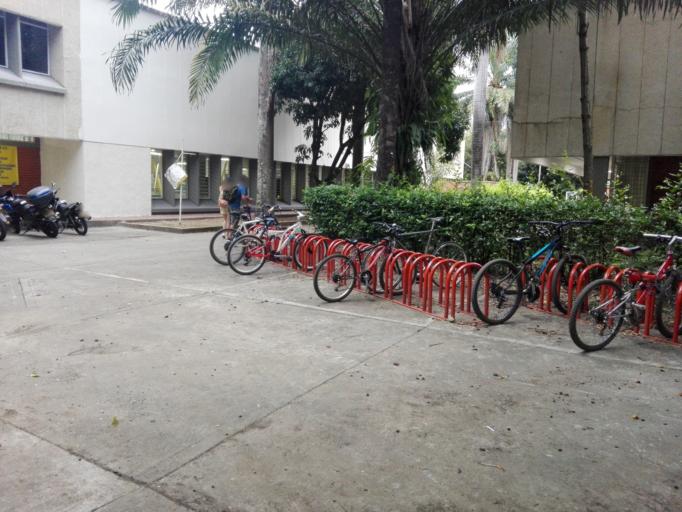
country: CO
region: Valle del Cauca
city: Cali
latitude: 3.3751
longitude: -76.5323
